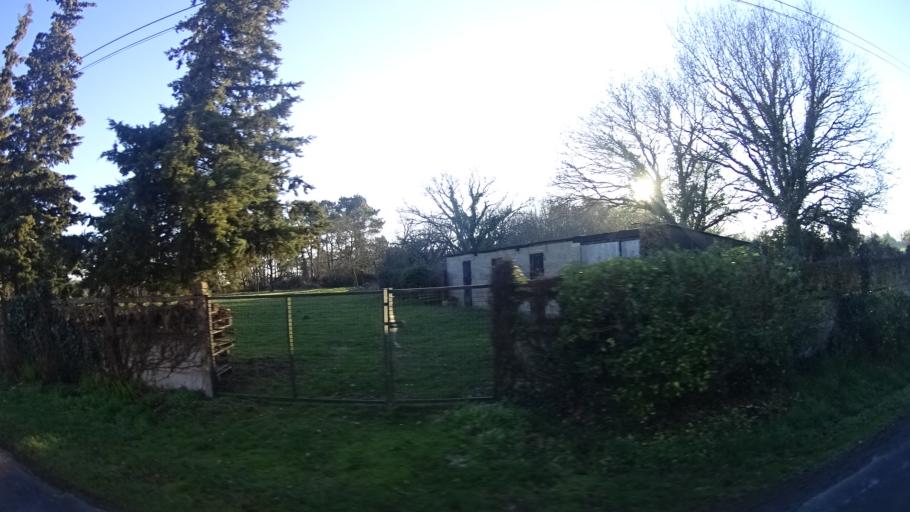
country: FR
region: Brittany
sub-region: Departement du Morbihan
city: Saint-Jean-la-Poterie
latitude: 47.6460
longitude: -2.1270
